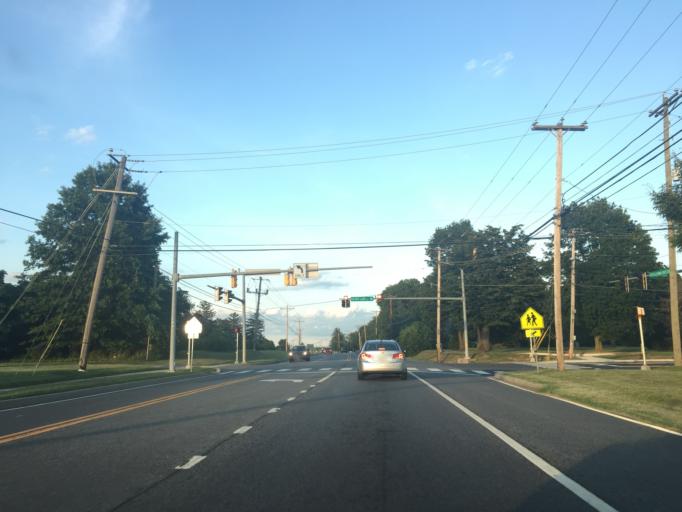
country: US
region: Delaware
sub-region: New Castle County
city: Middletown
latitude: 39.4507
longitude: -75.6975
